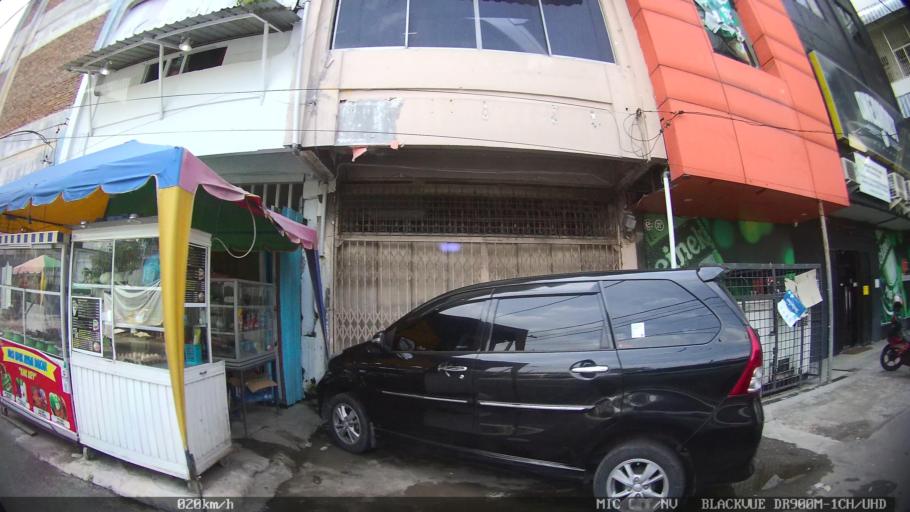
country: ID
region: North Sumatra
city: Medan
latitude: 3.5902
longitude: 98.6622
